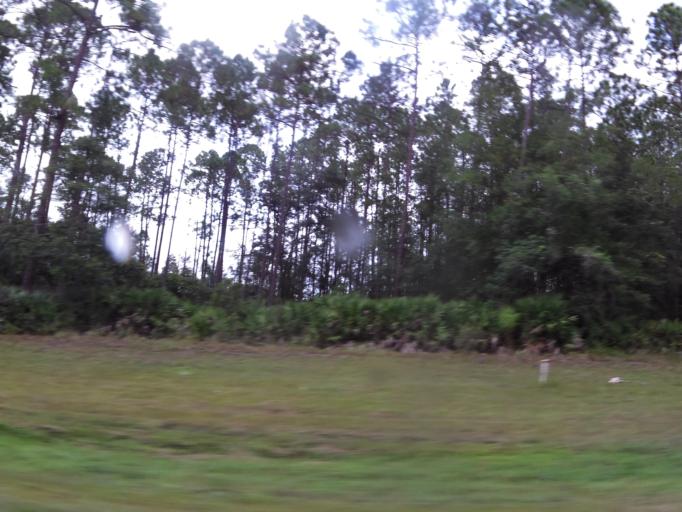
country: US
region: Florida
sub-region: Clay County
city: Middleburg
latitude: 30.0552
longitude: -81.8655
